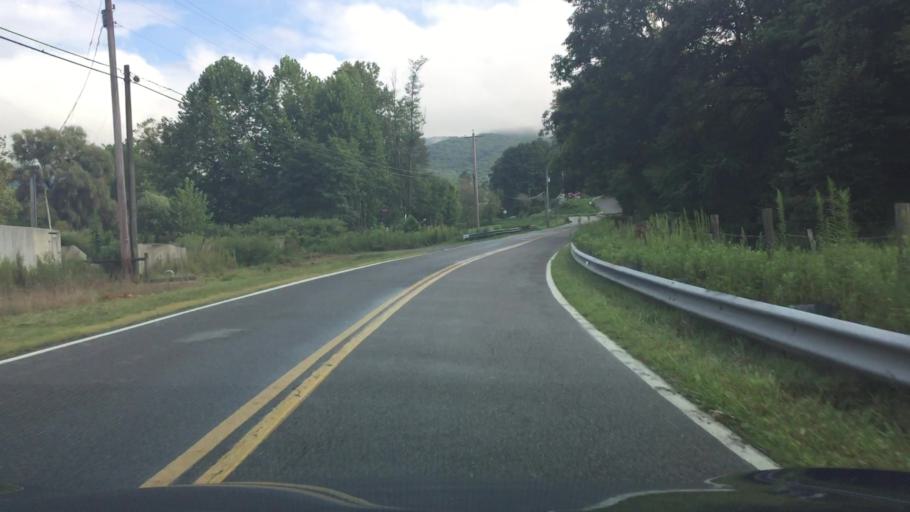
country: US
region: Virginia
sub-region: Smyth County
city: Atkins
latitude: 36.8541
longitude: -81.4280
